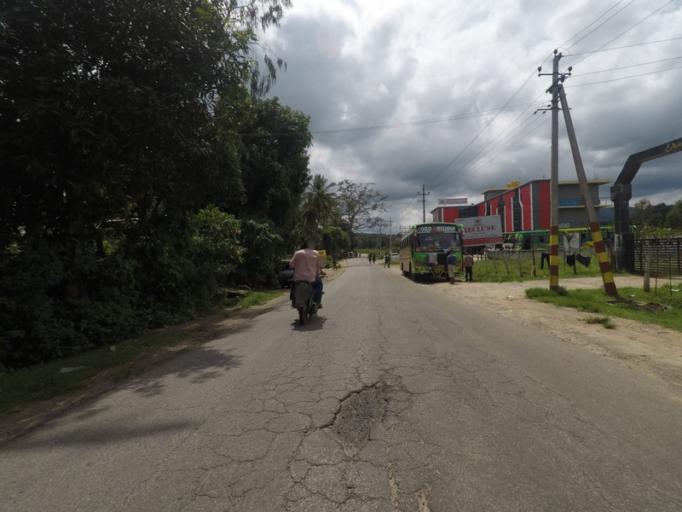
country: IN
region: Karnataka
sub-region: Kodagu
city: Kushalnagar
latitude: 12.4341
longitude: 75.9240
